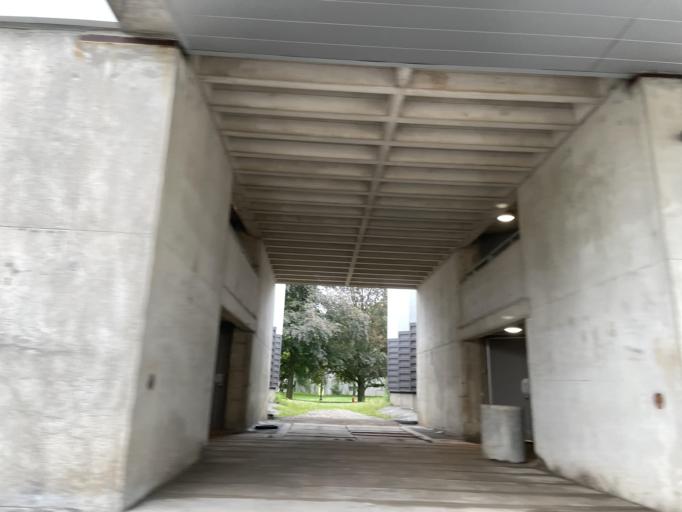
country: CA
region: Ontario
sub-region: Wellington County
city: Guelph
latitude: 43.5310
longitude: -80.2219
